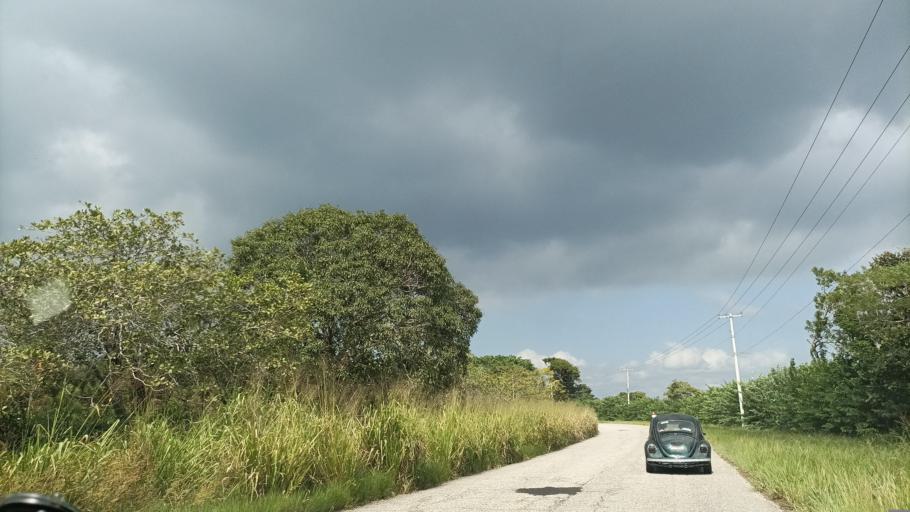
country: MX
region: Veracruz
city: Las Choapas
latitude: 17.8276
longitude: -94.1065
